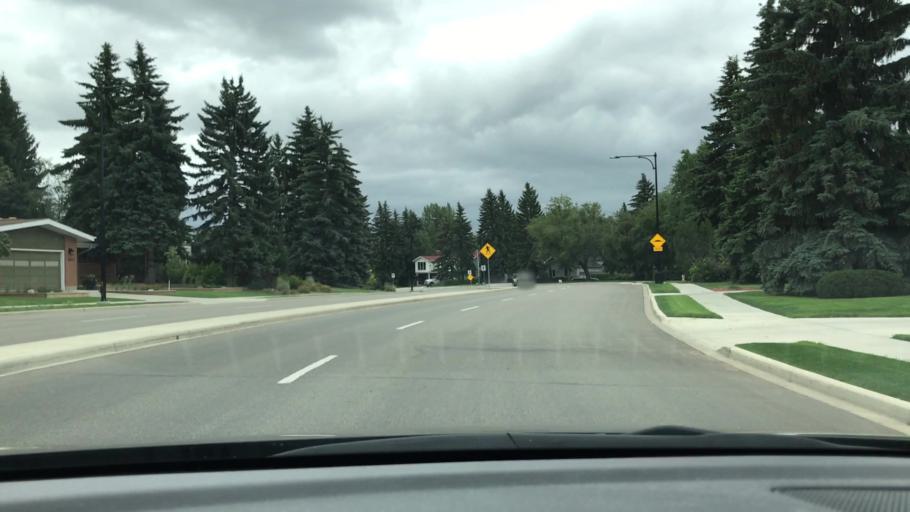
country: CA
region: Alberta
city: Edmonton
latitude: 53.5187
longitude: -113.5596
